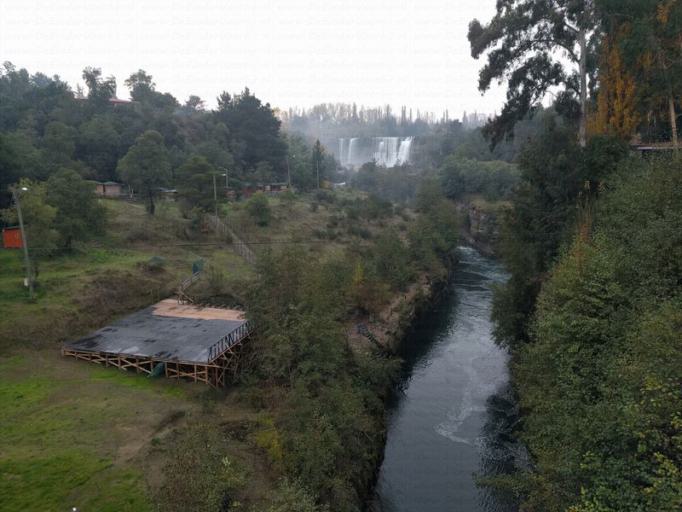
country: CL
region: Biobio
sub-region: Provincia de Biobio
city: Cabrero
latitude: -37.2192
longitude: -72.3835
